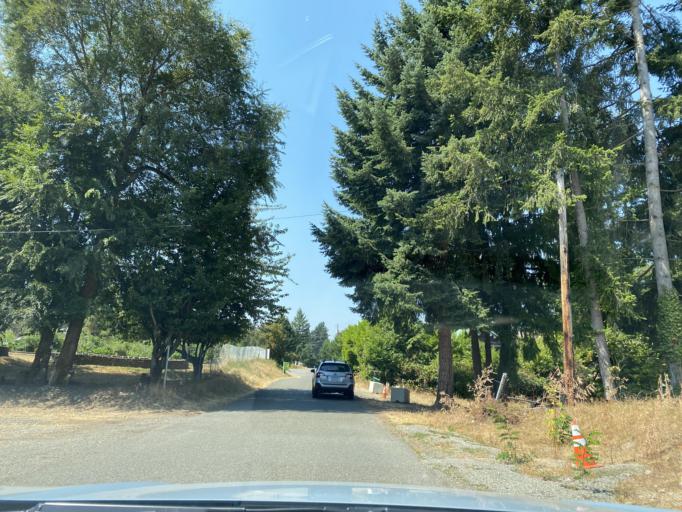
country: US
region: Washington
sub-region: Pierce County
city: Bonney Lake
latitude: 47.1768
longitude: -122.1816
